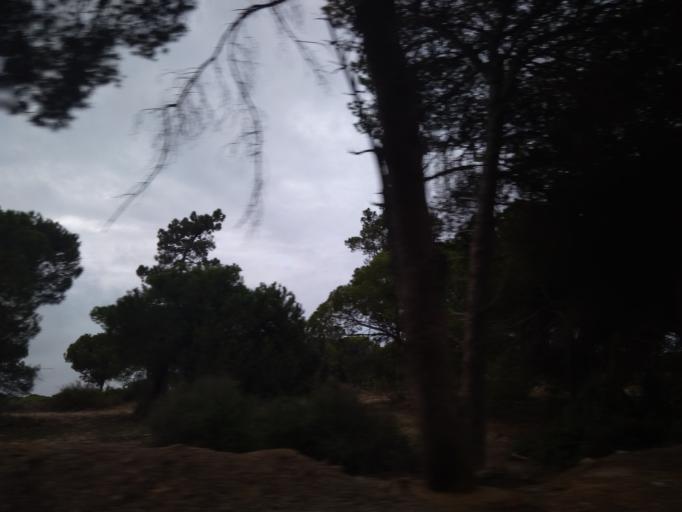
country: PT
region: Faro
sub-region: Faro
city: Faro
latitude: 37.0303
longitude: -7.9759
